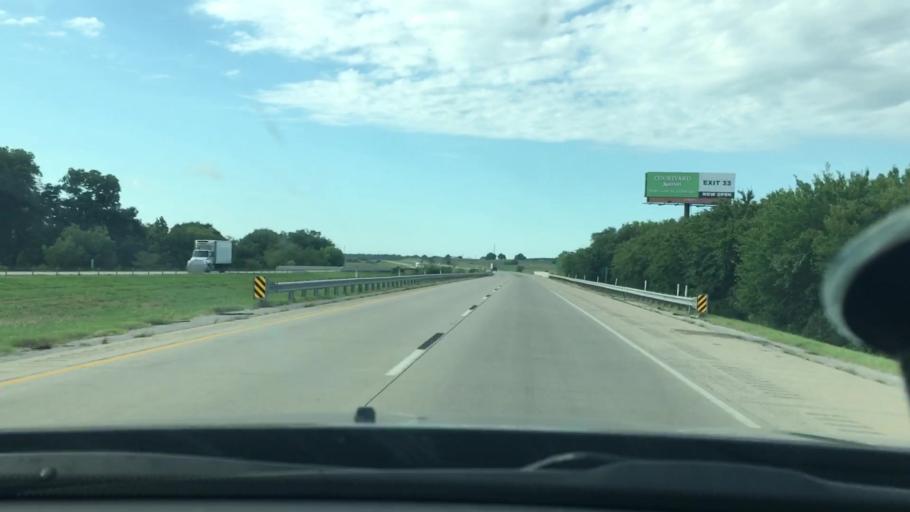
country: US
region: Oklahoma
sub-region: Carter County
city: Ardmore
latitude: 34.2657
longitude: -97.1642
